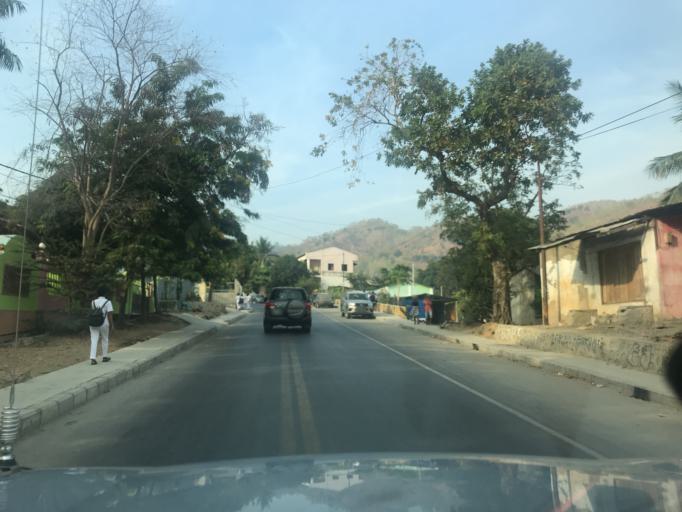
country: TL
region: Dili
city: Dili
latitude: -8.5703
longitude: 125.5836
